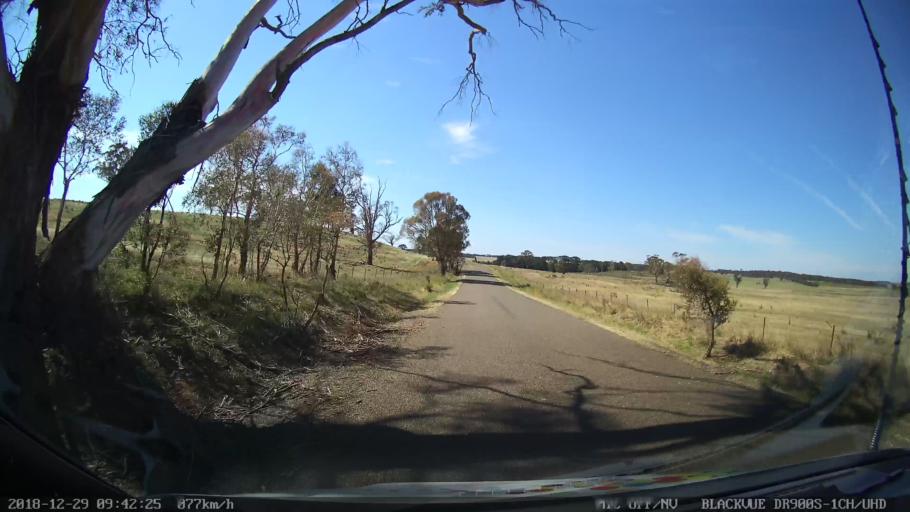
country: AU
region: New South Wales
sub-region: Upper Lachlan Shire
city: Crookwell
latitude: -34.6695
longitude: 149.4204
